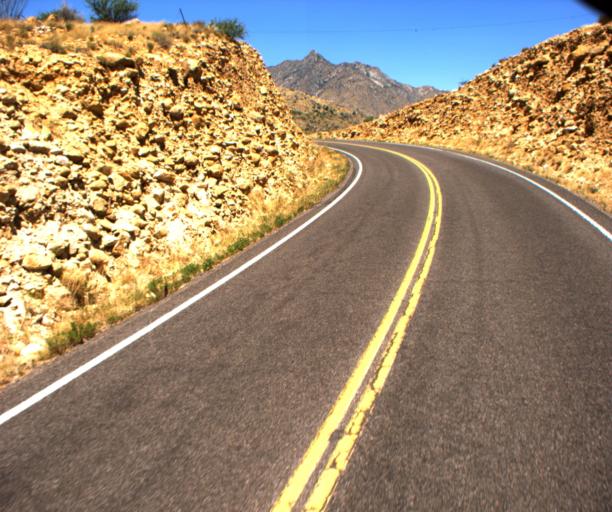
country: US
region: Arizona
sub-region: Graham County
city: Swift Trail Junction
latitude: 32.6898
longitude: -109.7604
